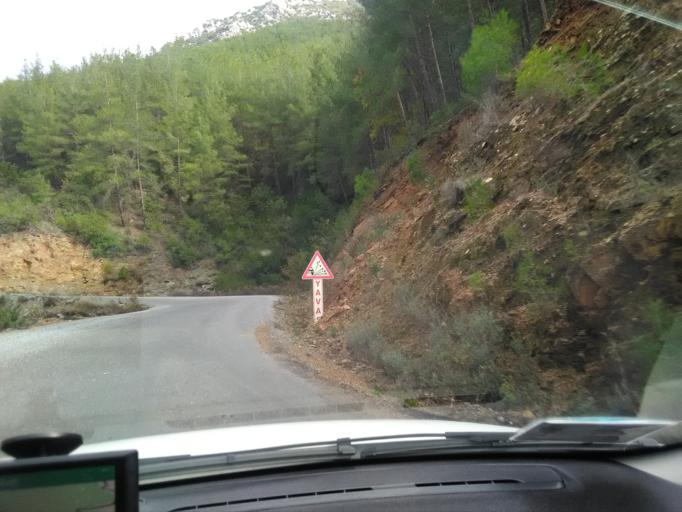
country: TR
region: Antalya
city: Gazipasa
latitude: 36.2398
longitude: 32.4196
